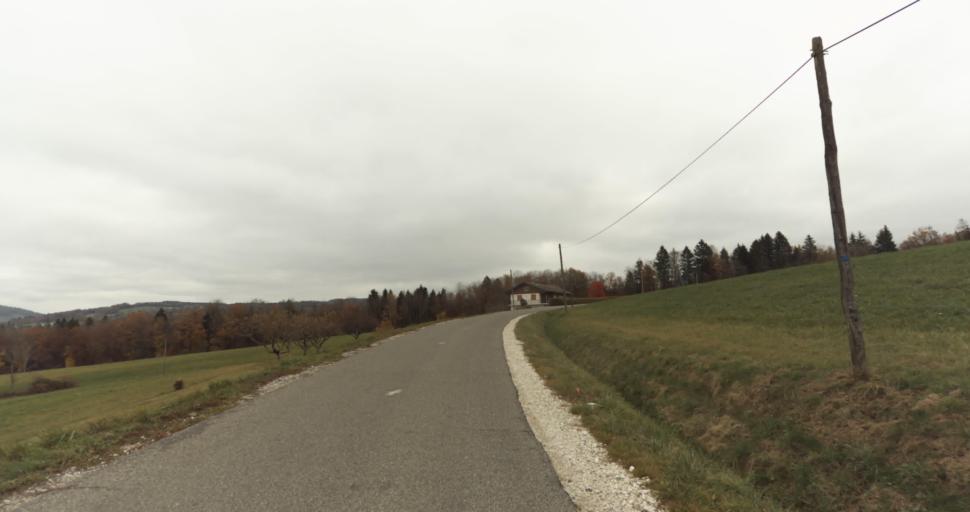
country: FR
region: Rhone-Alpes
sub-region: Departement de la Haute-Savoie
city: Groisy
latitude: 45.9947
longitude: 6.1924
